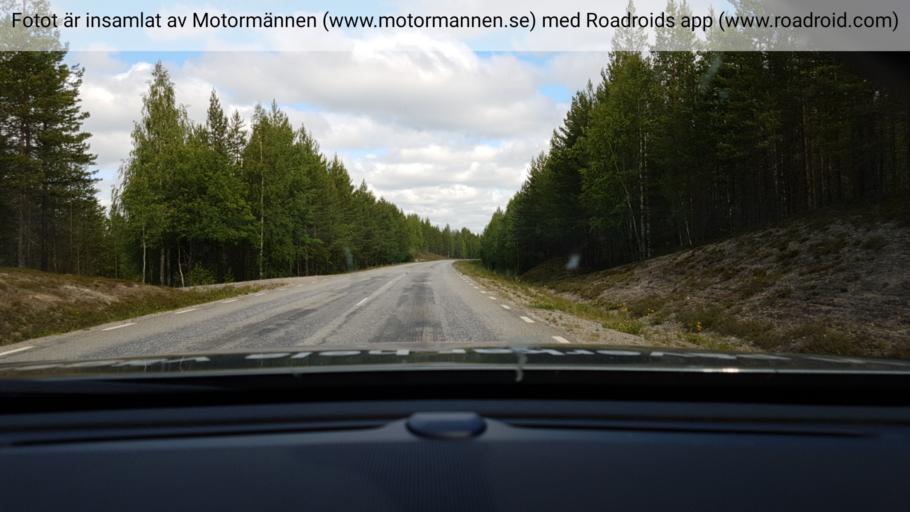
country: SE
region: Vaesterbotten
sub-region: Lycksele Kommun
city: Lycksele
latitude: 64.8408
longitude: 18.7668
